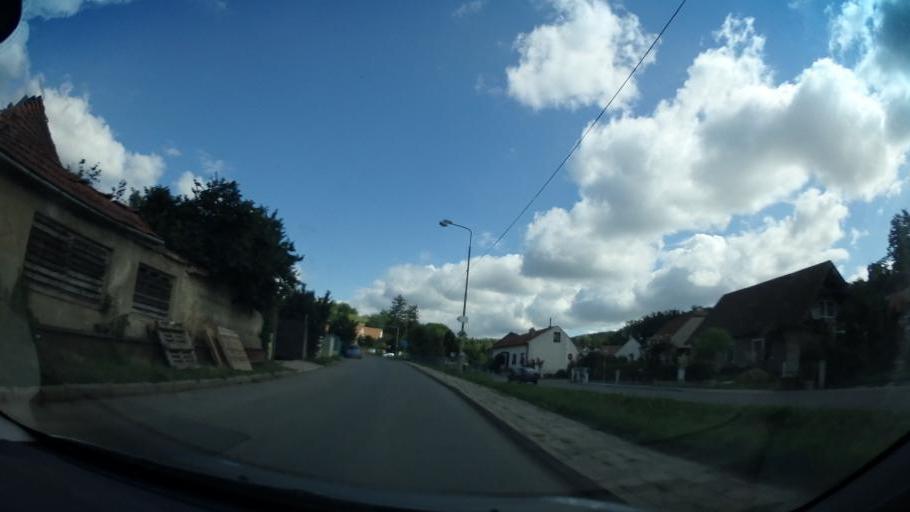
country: CZ
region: South Moravian
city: Dolni Kounice
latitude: 49.0834
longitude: 16.4379
